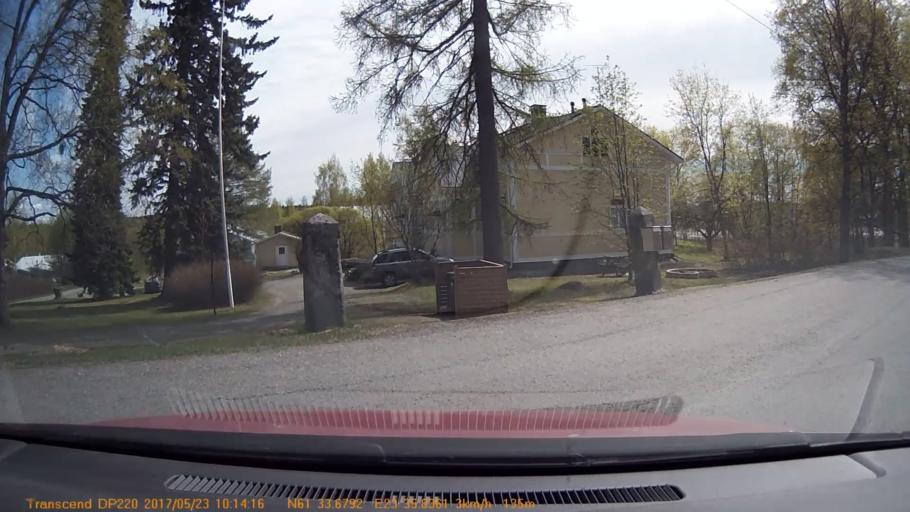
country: FI
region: Pirkanmaa
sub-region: Tampere
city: Yloejaervi
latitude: 61.5613
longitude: 23.5973
